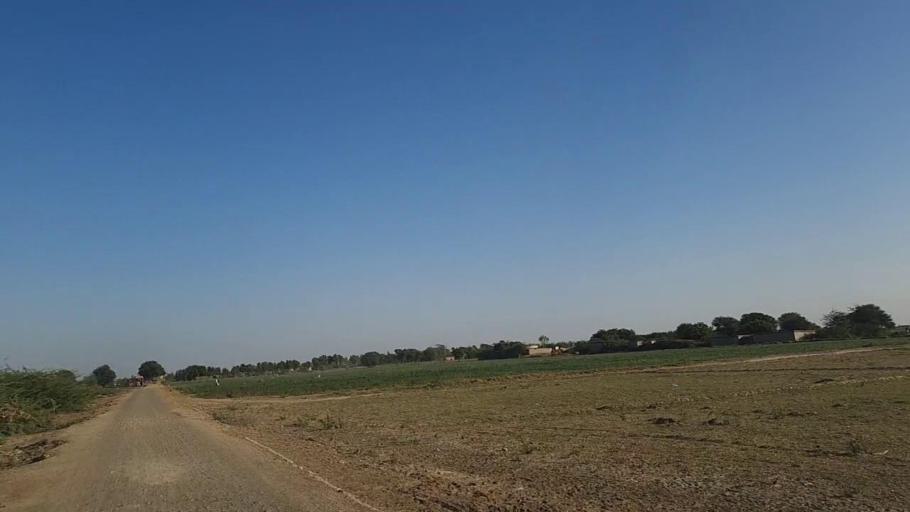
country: PK
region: Sindh
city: Naukot
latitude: 24.9514
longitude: 69.3873
